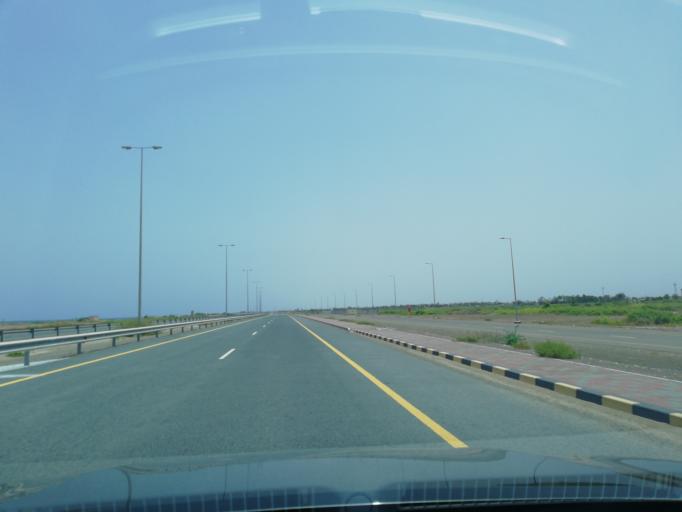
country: OM
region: Al Batinah
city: Shinas
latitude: 24.8511
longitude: 56.4202
